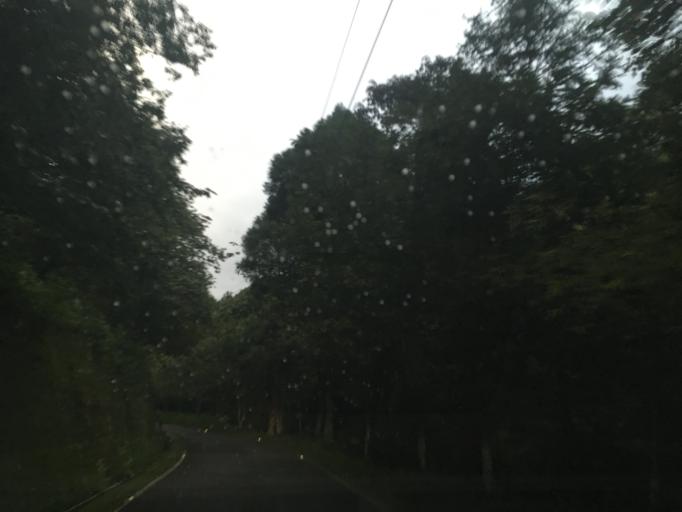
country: TW
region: Taiwan
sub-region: Nantou
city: Puli
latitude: 23.9049
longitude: 120.9093
